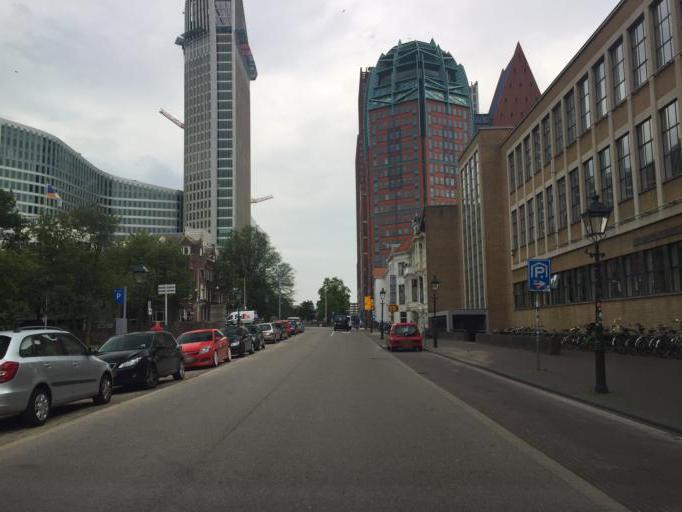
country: NL
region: South Holland
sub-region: Gemeente Den Haag
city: The Hague
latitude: 52.0819
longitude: 4.3193
